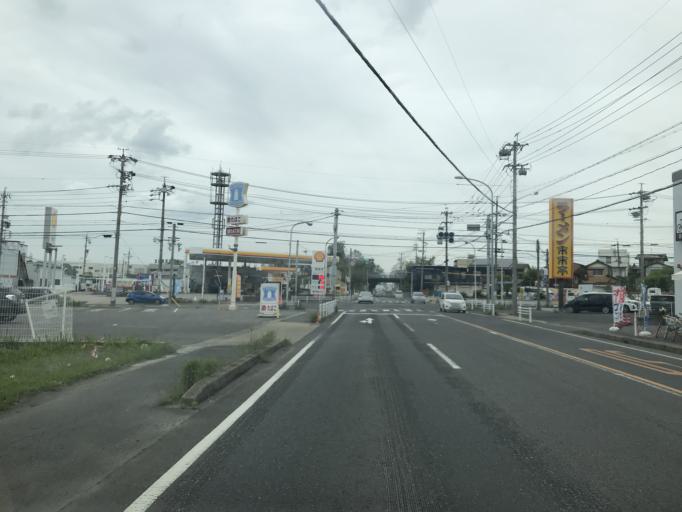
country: JP
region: Aichi
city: Kasugai
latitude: 35.2764
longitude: 136.9721
